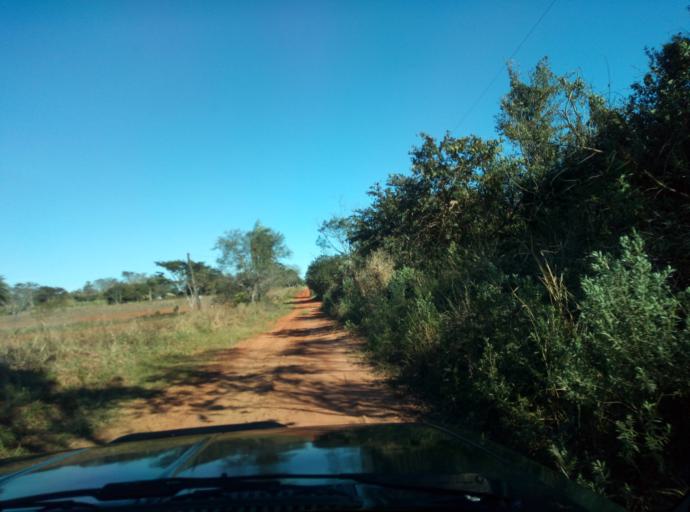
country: PY
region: Caaguazu
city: Doctor Cecilio Baez
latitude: -25.1790
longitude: -56.2392
